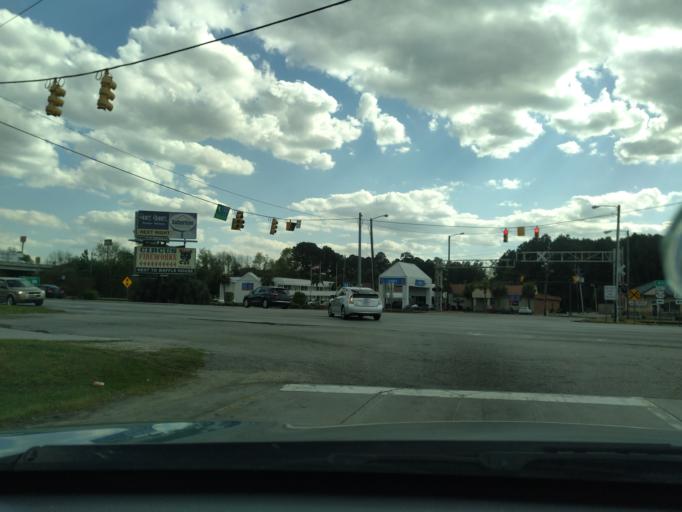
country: US
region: South Carolina
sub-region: Florence County
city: Florence
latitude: 34.2310
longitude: -79.8006
